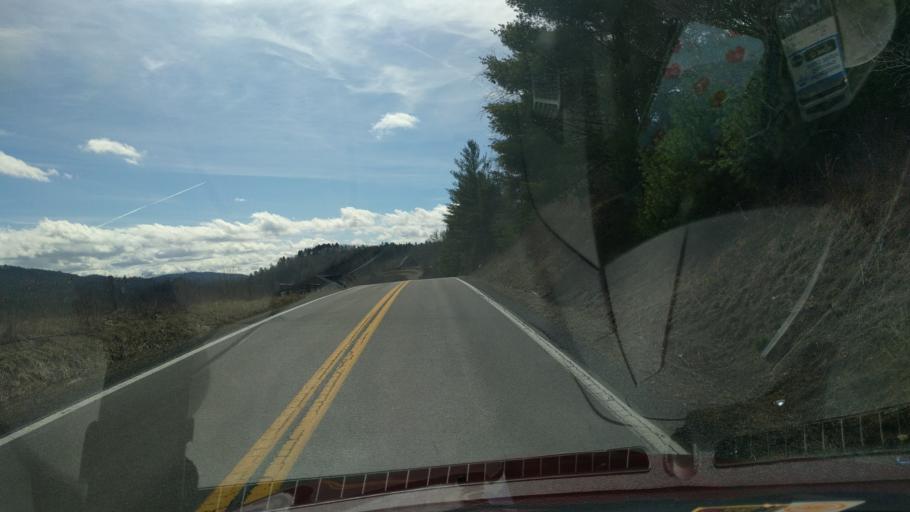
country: US
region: West Virginia
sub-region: Pocahontas County
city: Marlinton
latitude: 38.2197
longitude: -79.9218
